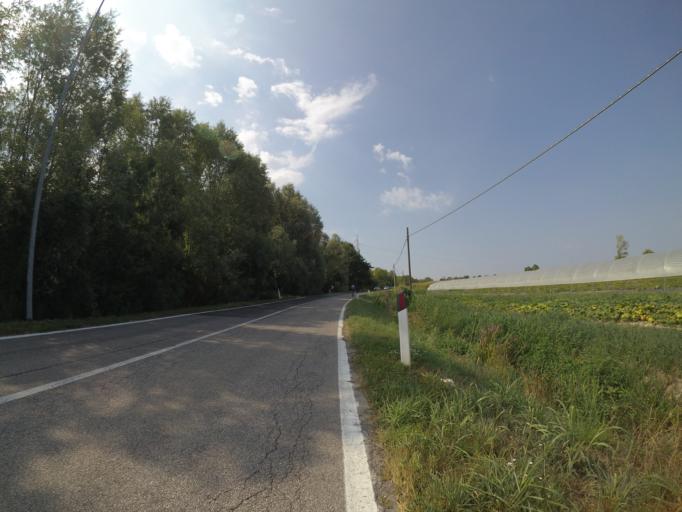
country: IT
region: Friuli Venezia Giulia
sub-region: Provincia di Udine
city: Precenicco
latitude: 45.7732
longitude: 13.0760
